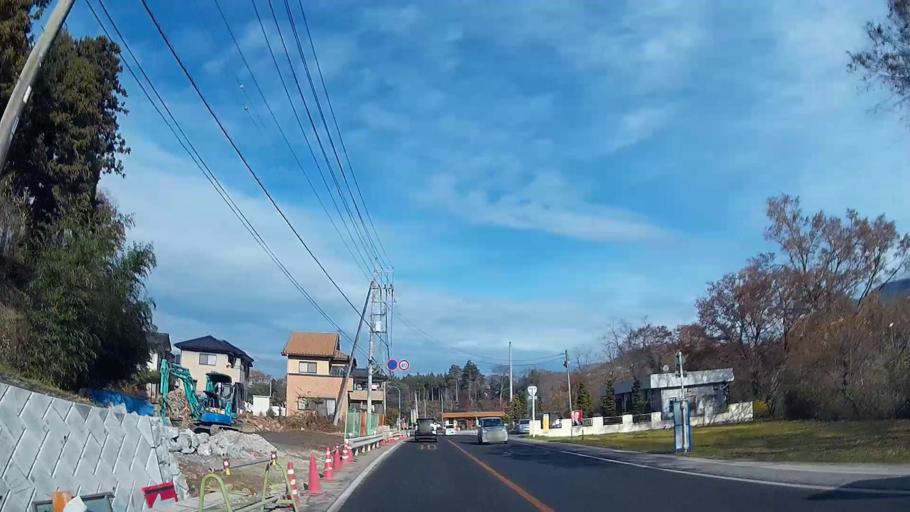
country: JP
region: Saitama
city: Chichibu
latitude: 35.9844
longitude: 139.1064
